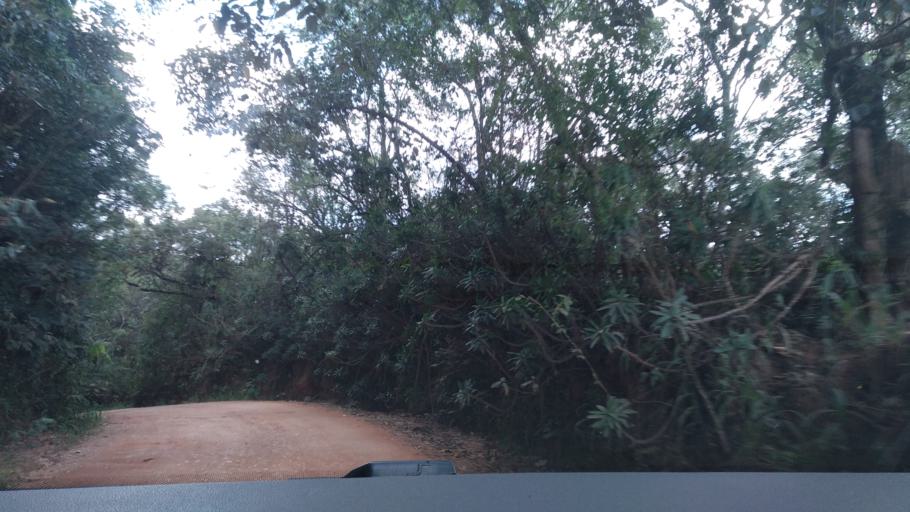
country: BR
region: Sao Paulo
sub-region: Cajamar
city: Cajamar
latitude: -23.2848
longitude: -46.8896
